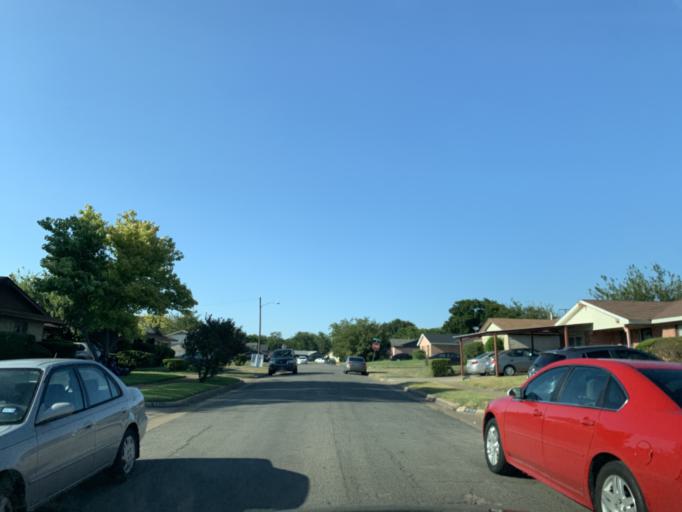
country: US
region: Texas
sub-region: Dallas County
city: Hutchins
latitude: 32.6629
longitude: -96.7669
